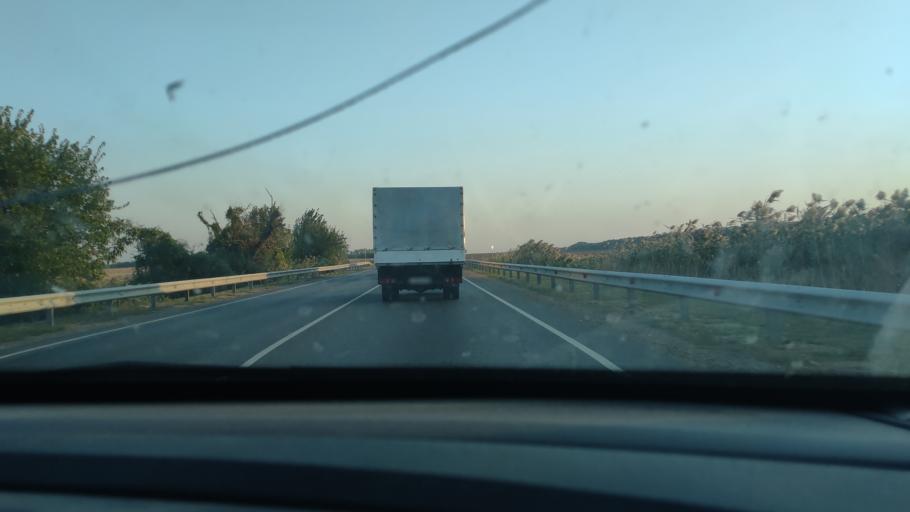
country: RU
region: Krasnodarskiy
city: Bryukhovetskaya
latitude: 45.7568
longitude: 38.9880
